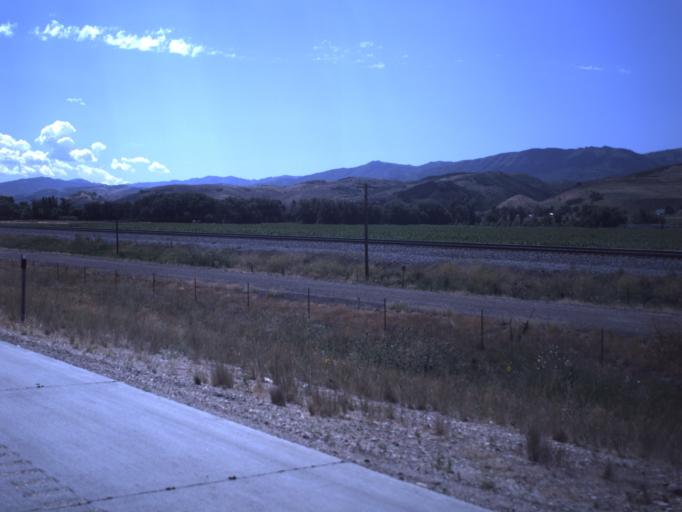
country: US
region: Utah
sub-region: Morgan County
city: Mountain Green
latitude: 41.0958
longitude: -111.7401
